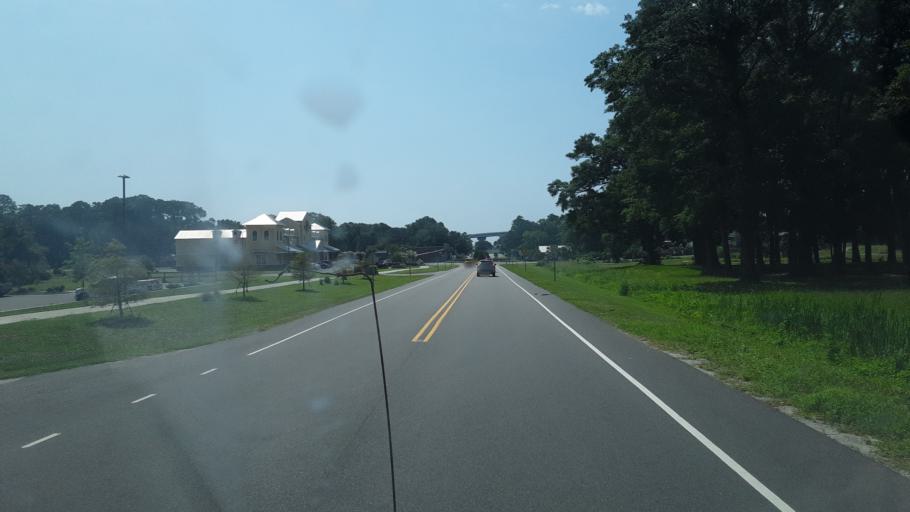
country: US
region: North Carolina
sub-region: Brunswick County
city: Sunset Beach
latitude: 33.8878
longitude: -78.5109
